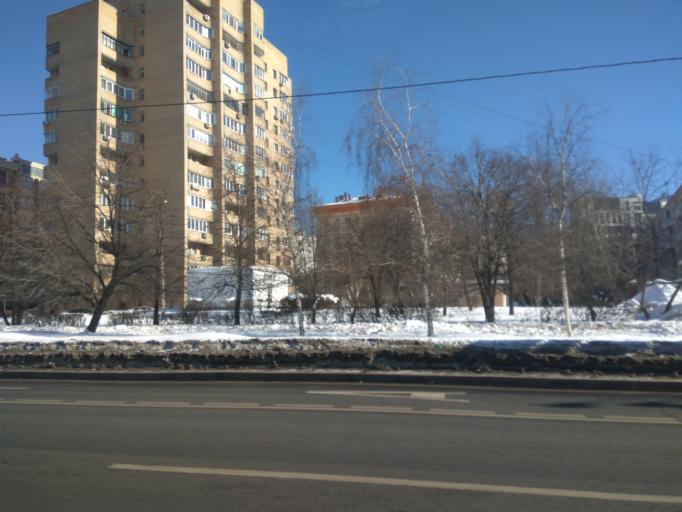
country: RU
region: Moscow
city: Taganskiy
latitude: 55.7325
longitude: 37.6594
